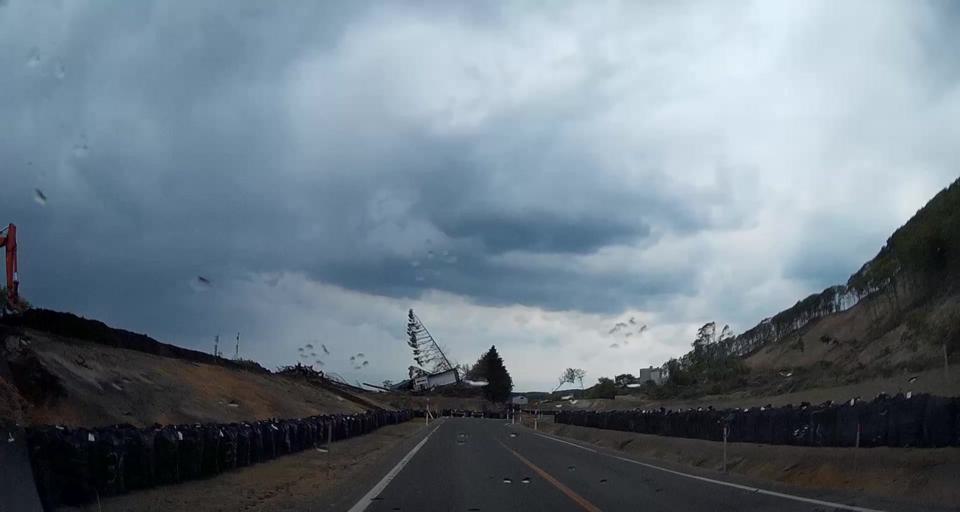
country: JP
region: Hokkaido
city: Chitose
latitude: 42.7559
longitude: 141.9435
